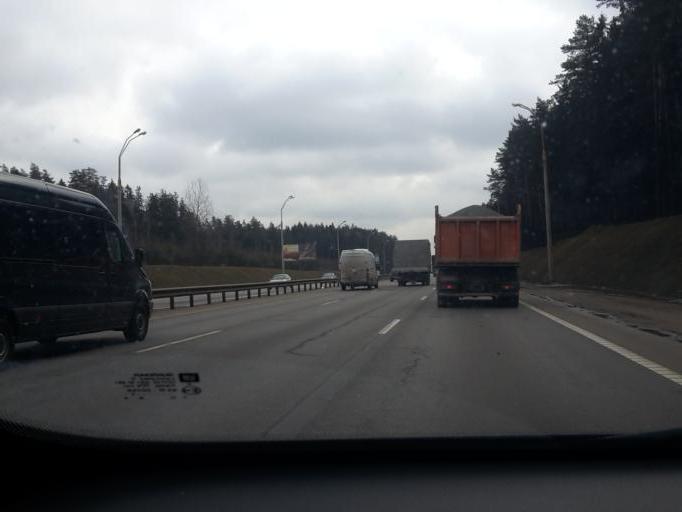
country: BY
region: Minsk
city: Borovlyany
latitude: 53.9517
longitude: 27.6514
